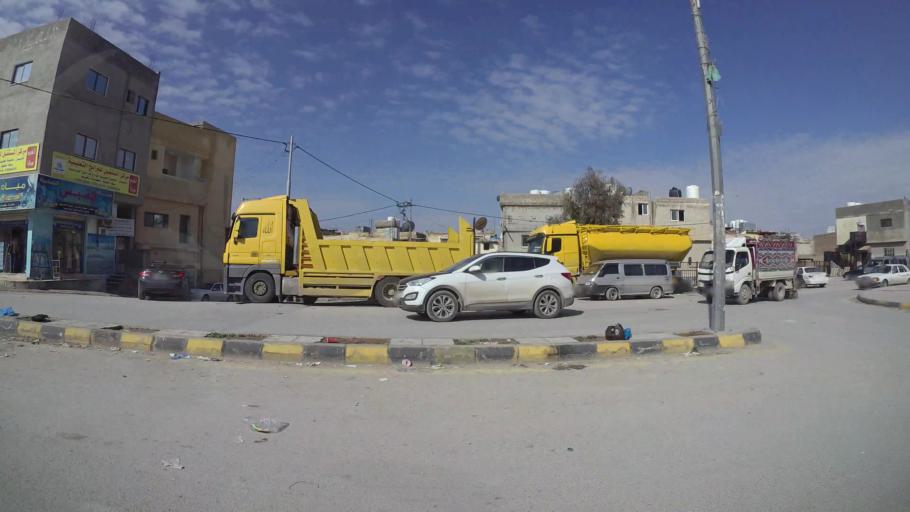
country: JO
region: Amman
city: Al Jubayhah
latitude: 32.0687
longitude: 35.8430
